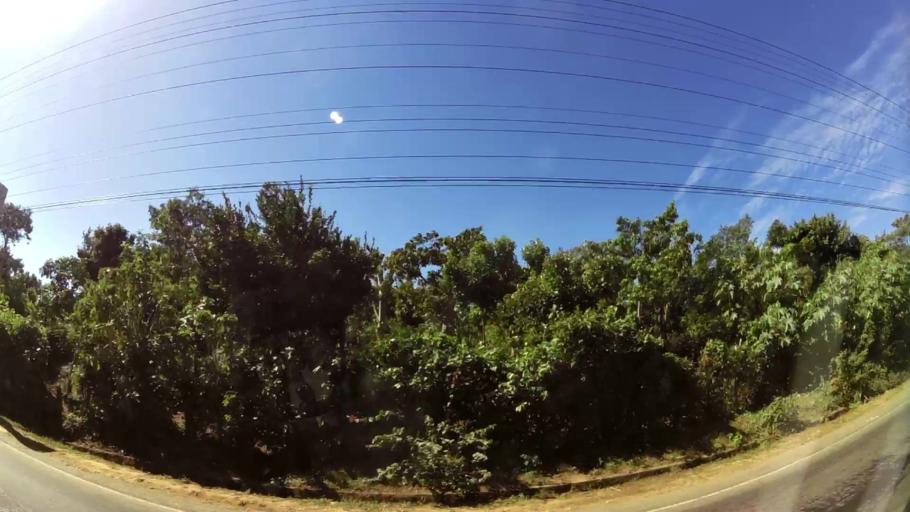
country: SV
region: Sonsonate
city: Juayua
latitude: 13.8341
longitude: -89.7616
